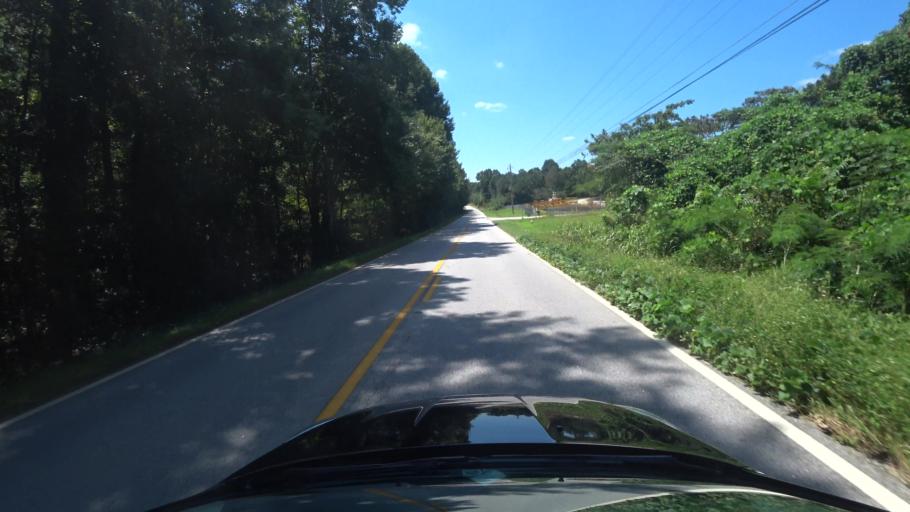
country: US
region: Georgia
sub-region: Newton County
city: Oxford
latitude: 33.6329
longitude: -83.8216
